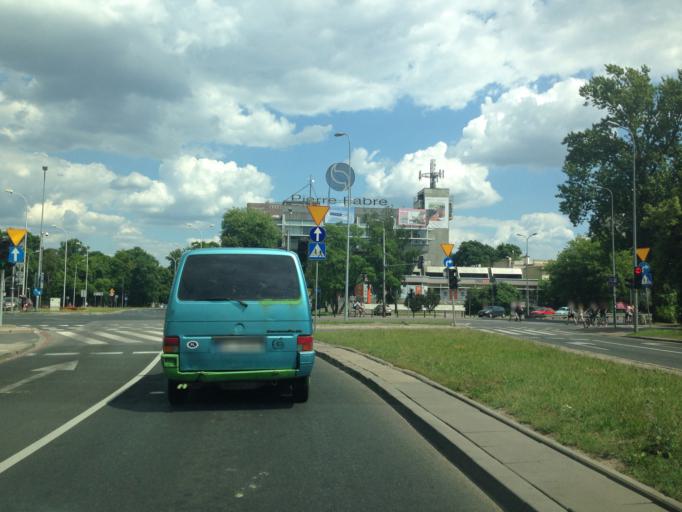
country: PL
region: Masovian Voivodeship
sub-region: Warszawa
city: Mokotow
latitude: 52.2068
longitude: 21.0303
